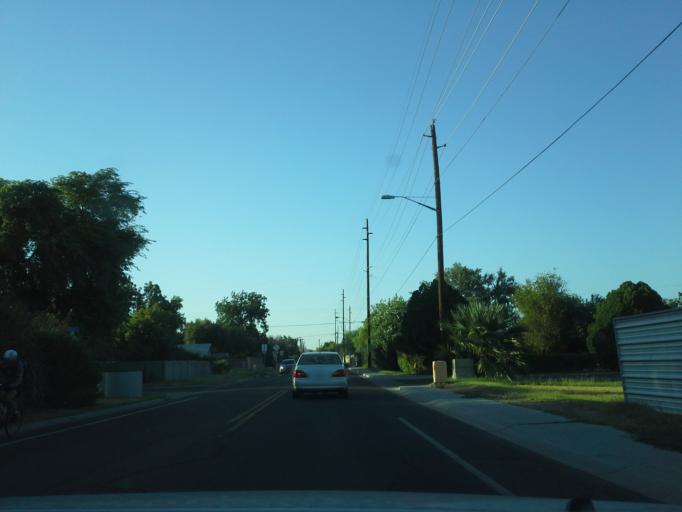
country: US
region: Arizona
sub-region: Maricopa County
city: Phoenix
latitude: 33.5008
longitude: -112.0781
